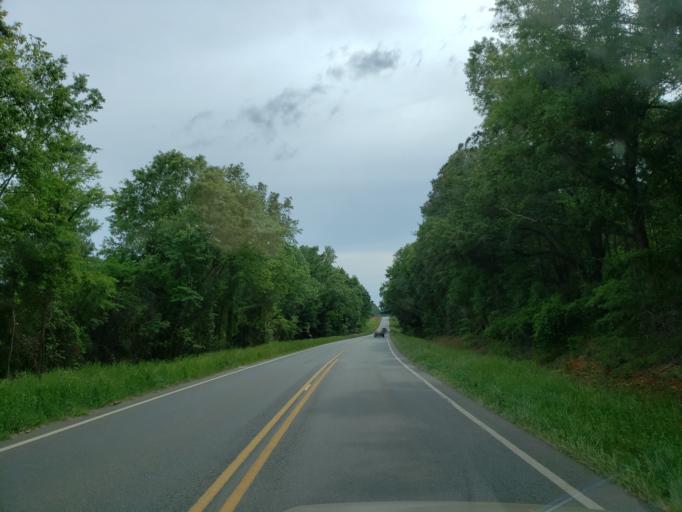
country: US
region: Georgia
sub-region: Macon County
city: Marshallville
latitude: 32.3868
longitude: -83.8694
